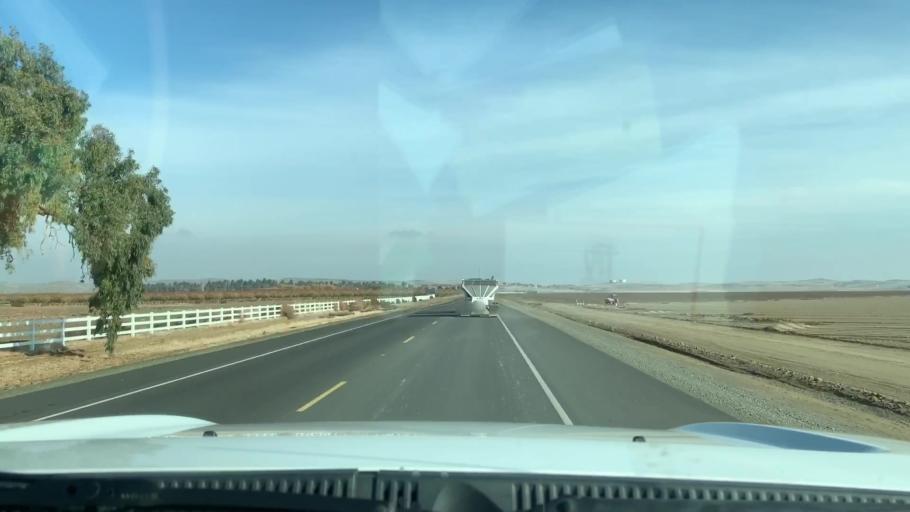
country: US
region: California
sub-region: Fresno County
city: Coalinga
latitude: 36.1853
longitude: -120.3483
